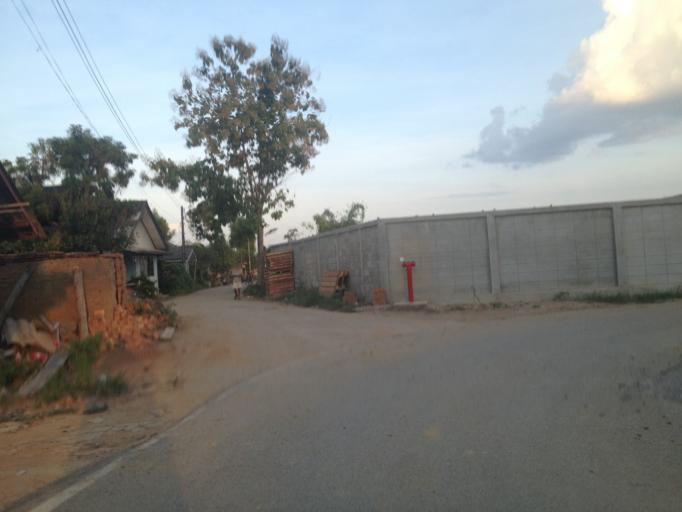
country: TH
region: Chiang Mai
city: Chiang Mai
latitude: 18.7626
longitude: 98.9592
